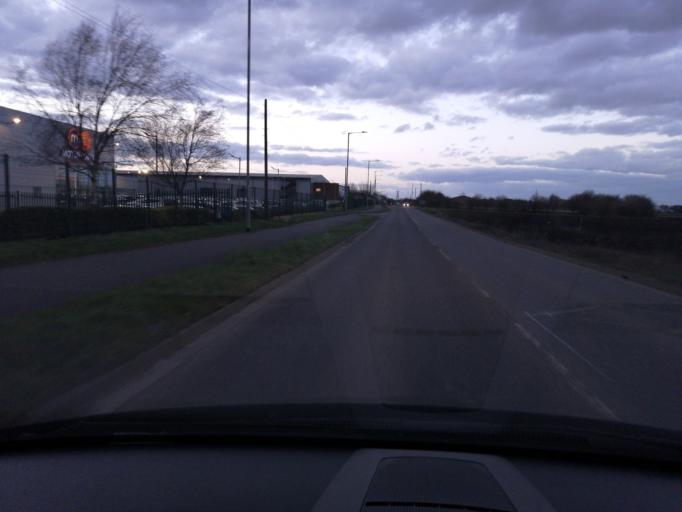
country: GB
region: England
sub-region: Peterborough
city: Eye
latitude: 52.5801
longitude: -0.2038
